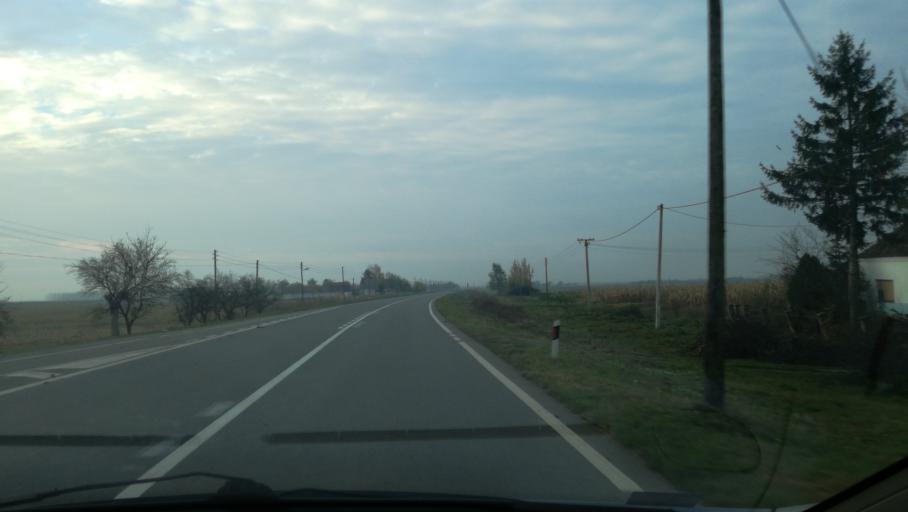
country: RS
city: Banatska Topola
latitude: 45.6856
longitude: 20.4234
